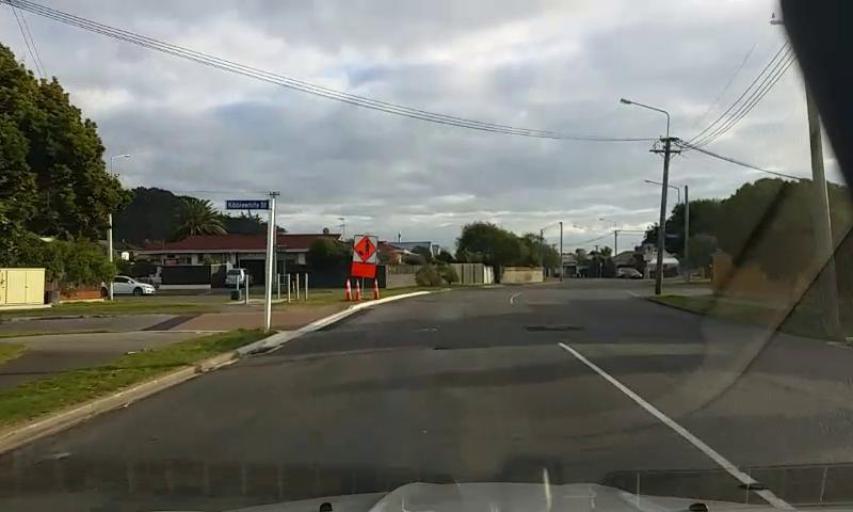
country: NZ
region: Canterbury
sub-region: Christchurch City
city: Christchurch
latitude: -43.5196
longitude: 172.7310
